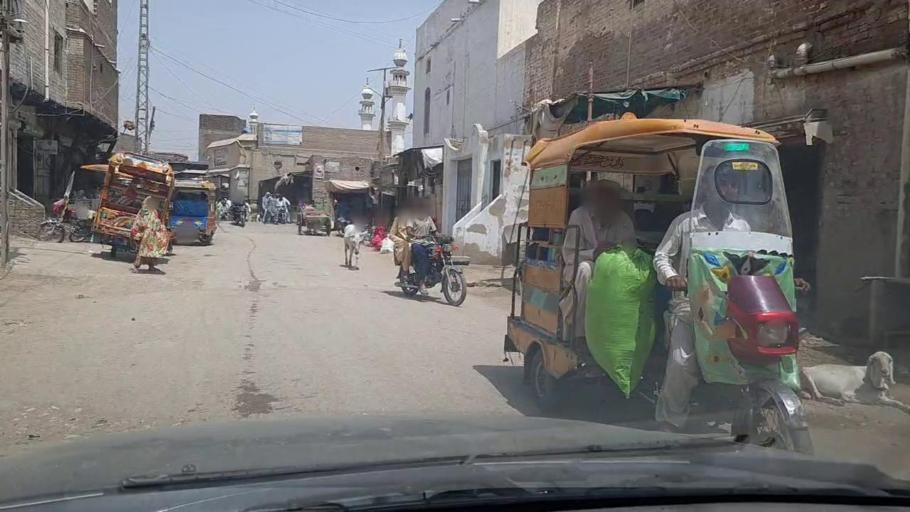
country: PK
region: Sindh
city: Ratodero
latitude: 27.8017
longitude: 68.2871
